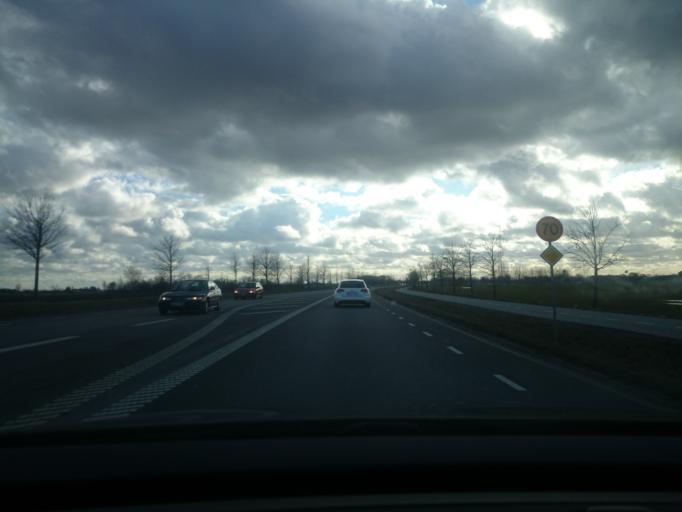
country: SE
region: Skane
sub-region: Staffanstorps Kommun
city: Hjaerup
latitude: 55.6707
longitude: 13.1632
